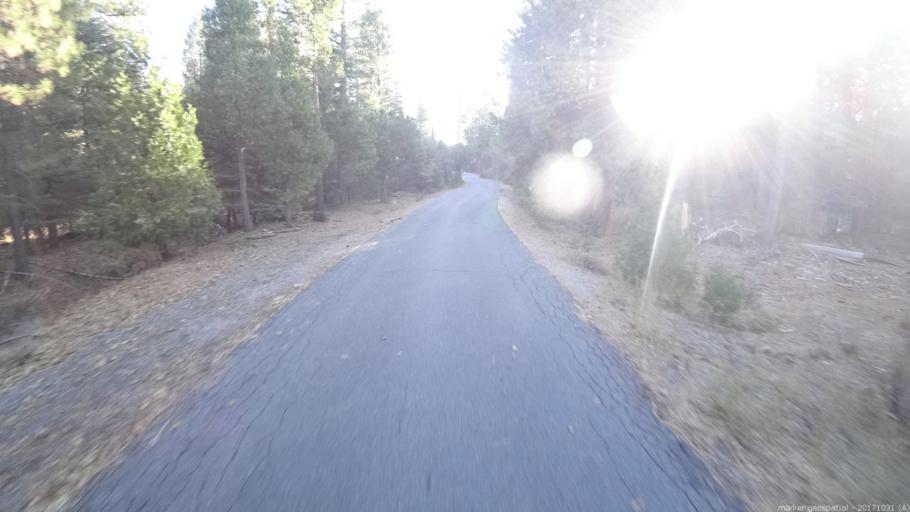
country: US
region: California
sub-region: Shasta County
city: Shingletown
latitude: 40.5238
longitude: -121.7928
